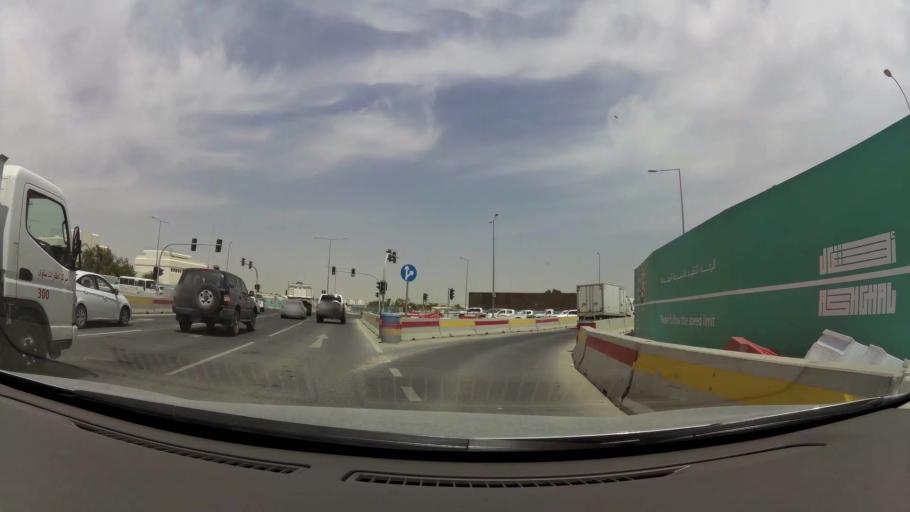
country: QA
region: Baladiyat ar Rayyan
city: Ar Rayyan
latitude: 25.3061
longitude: 51.4124
